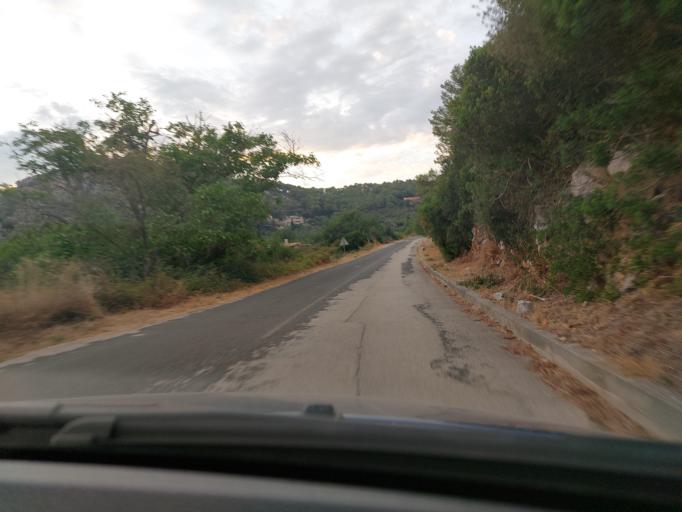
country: HR
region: Dubrovacko-Neretvanska
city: Smokvica
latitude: 42.7624
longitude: 16.8968
